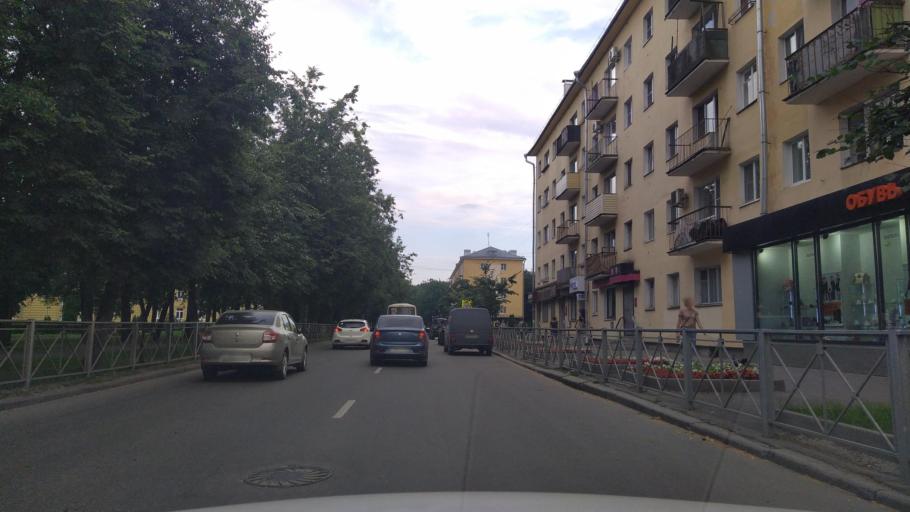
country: RU
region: Novgorod
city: Velikiy Novgorod
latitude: 58.5229
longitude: 31.2656
